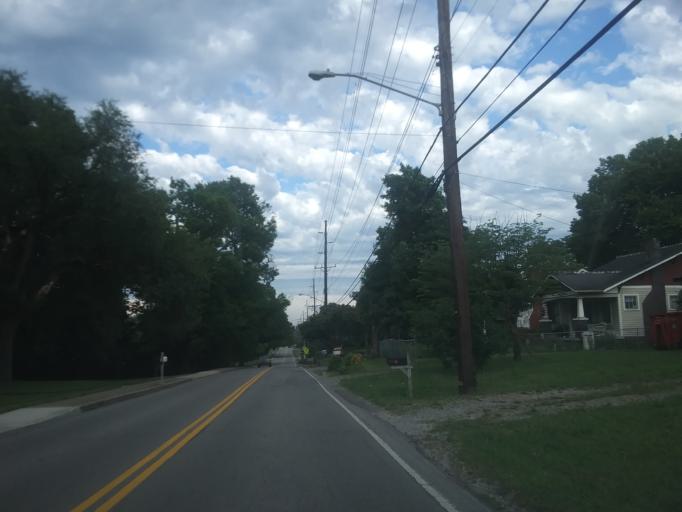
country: US
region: Tennessee
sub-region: Davidson County
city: Oak Hill
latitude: 36.0994
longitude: -86.7371
